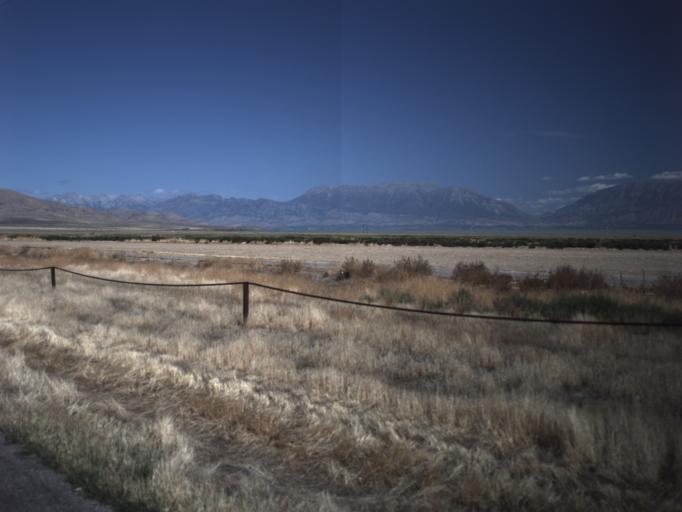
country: US
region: Utah
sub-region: Utah County
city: Genola
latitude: 40.1100
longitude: -111.9591
